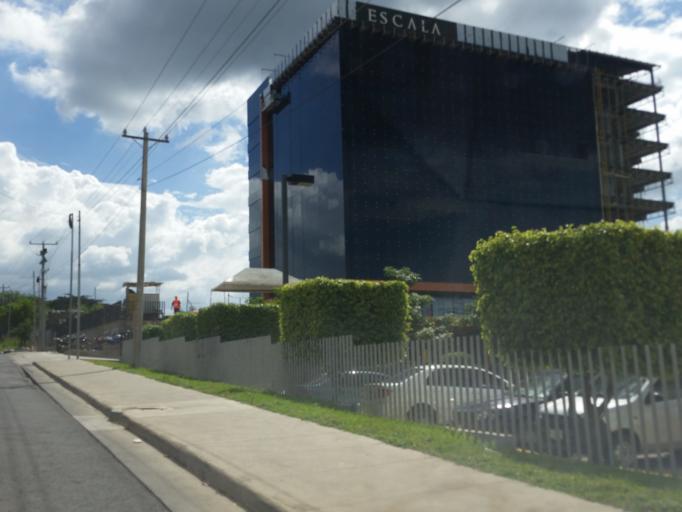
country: NI
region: Managua
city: Managua
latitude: 12.1020
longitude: -86.2583
